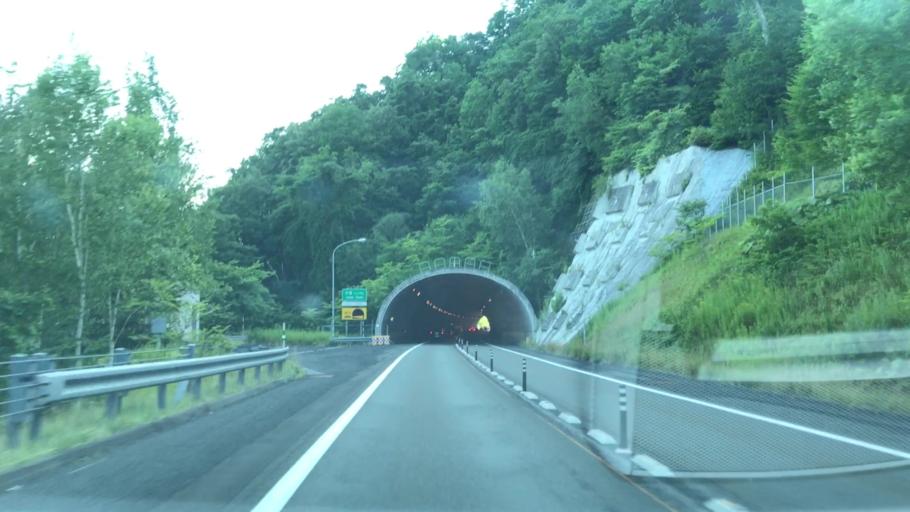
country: JP
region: Hokkaido
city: Chitose
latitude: 42.9087
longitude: 142.0131
